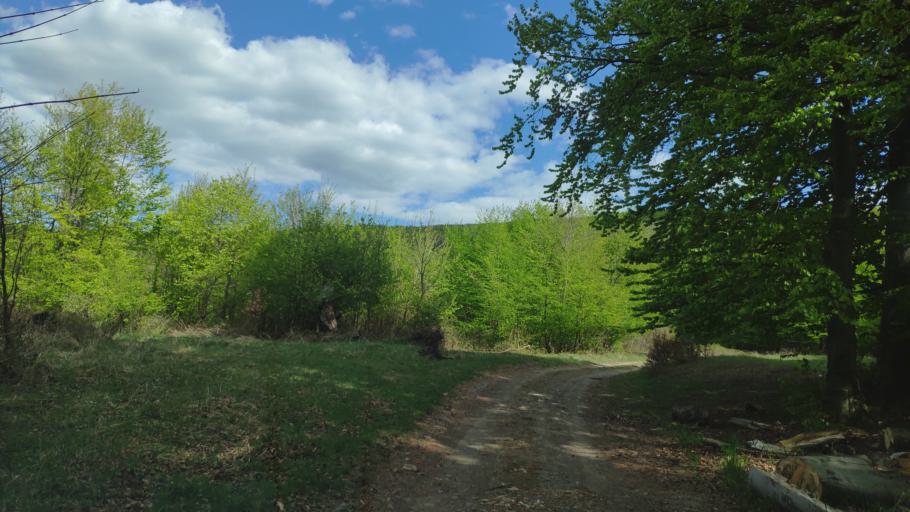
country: SK
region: Kosicky
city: Kosice
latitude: 48.6591
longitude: 21.4434
